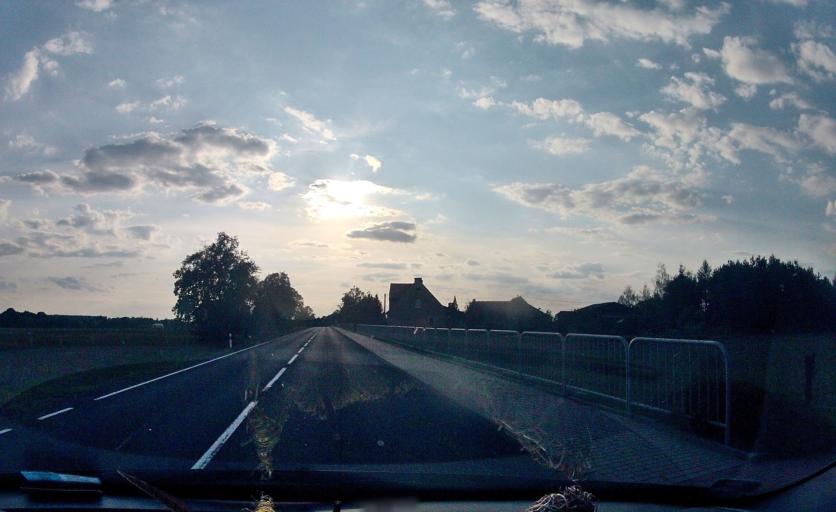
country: PL
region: Opole Voivodeship
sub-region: Powiat oleski
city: Gorzow Slaski
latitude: 51.0022
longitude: 18.3273
